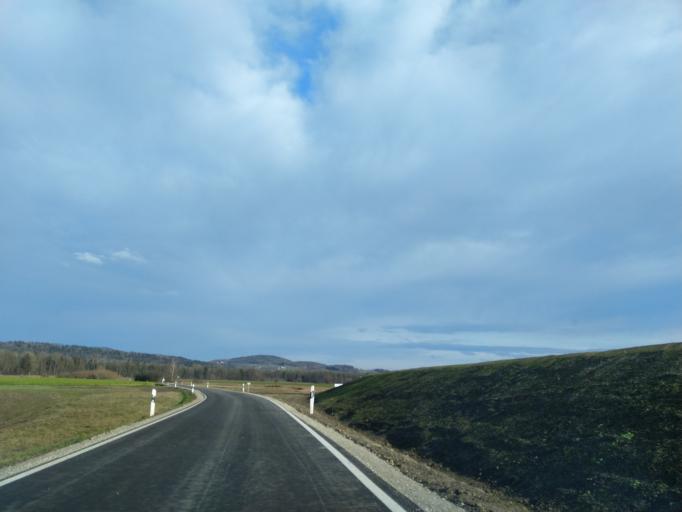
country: DE
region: Bavaria
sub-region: Lower Bavaria
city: Moos
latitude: 48.7834
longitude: 12.9685
